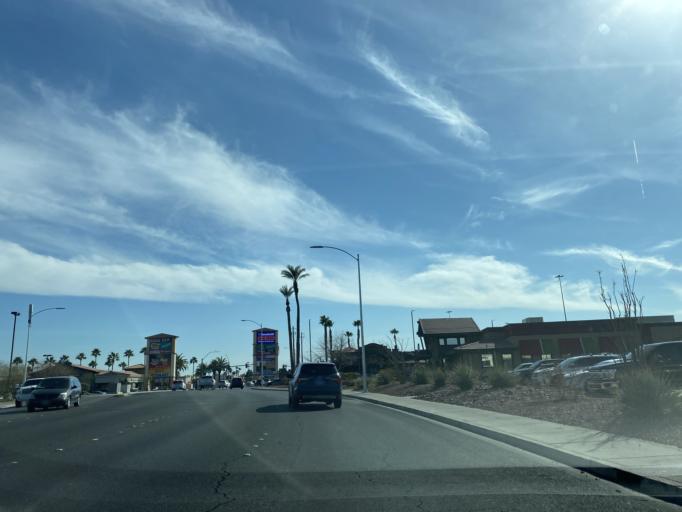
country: US
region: Nevada
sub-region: Clark County
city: Spring Valley
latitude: 36.1994
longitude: -115.2424
